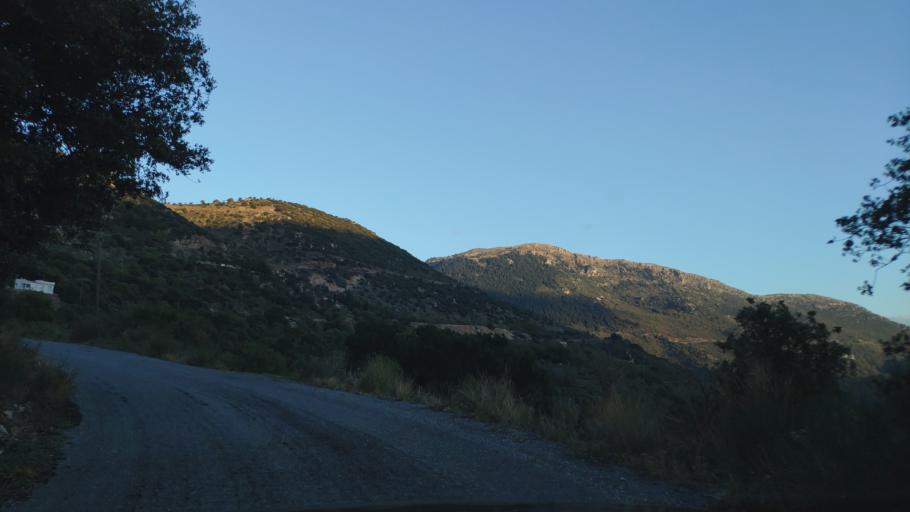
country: GR
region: Peloponnese
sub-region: Nomos Arkadias
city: Dimitsana
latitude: 37.5871
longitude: 22.0386
